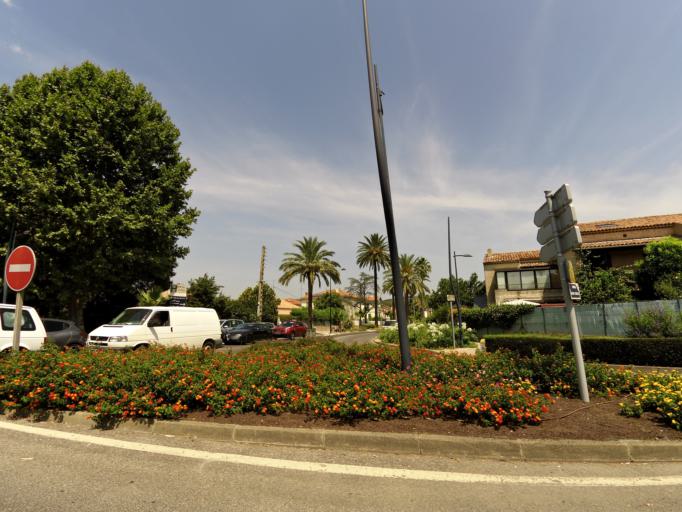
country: FR
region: Provence-Alpes-Cote d'Azur
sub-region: Departement du Var
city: Hyeres
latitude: 43.1136
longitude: 6.1238
